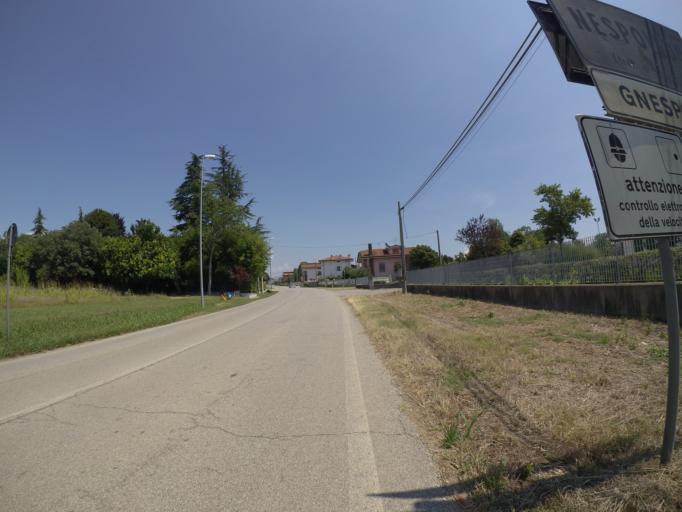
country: IT
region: Friuli Venezia Giulia
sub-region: Provincia di Udine
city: Basiliano
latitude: 45.9783
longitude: 13.0825
